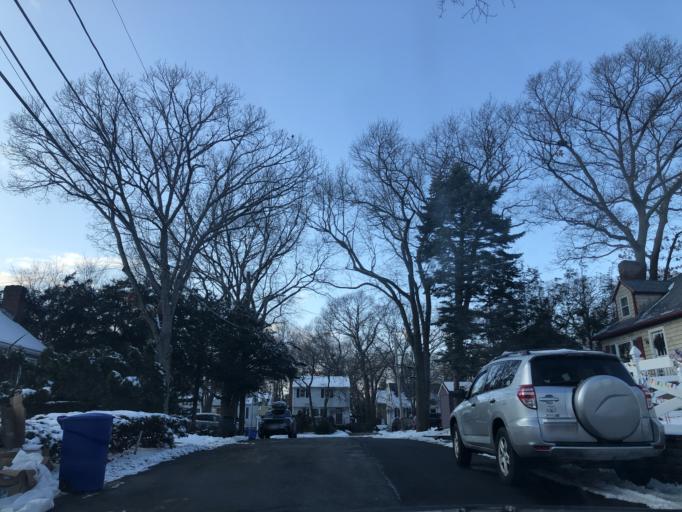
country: US
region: Massachusetts
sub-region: Middlesex County
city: Arlington
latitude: 42.4274
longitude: -71.1672
